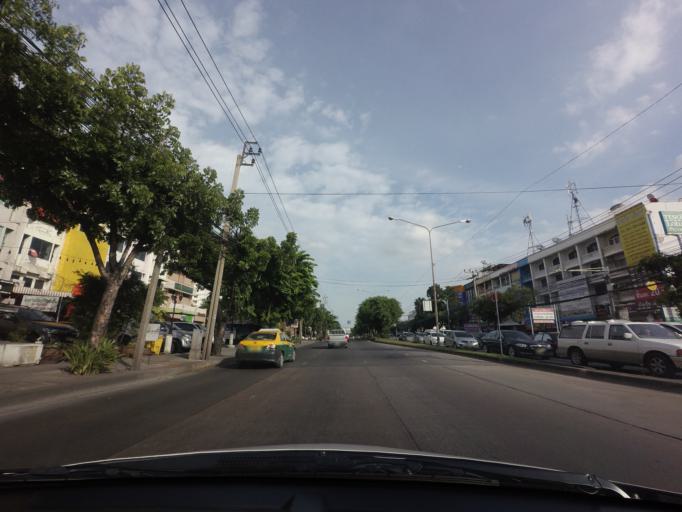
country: TH
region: Bangkok
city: Bueng Kum
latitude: 13.8017
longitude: 100.6484
